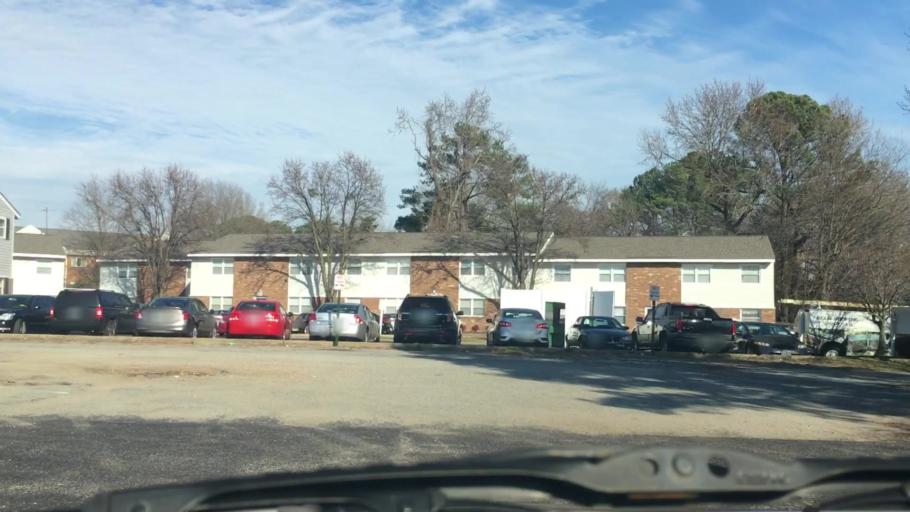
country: US
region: Virginia
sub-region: City of Norfolk
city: Norfolk
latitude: 36.8857
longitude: -76.2588
